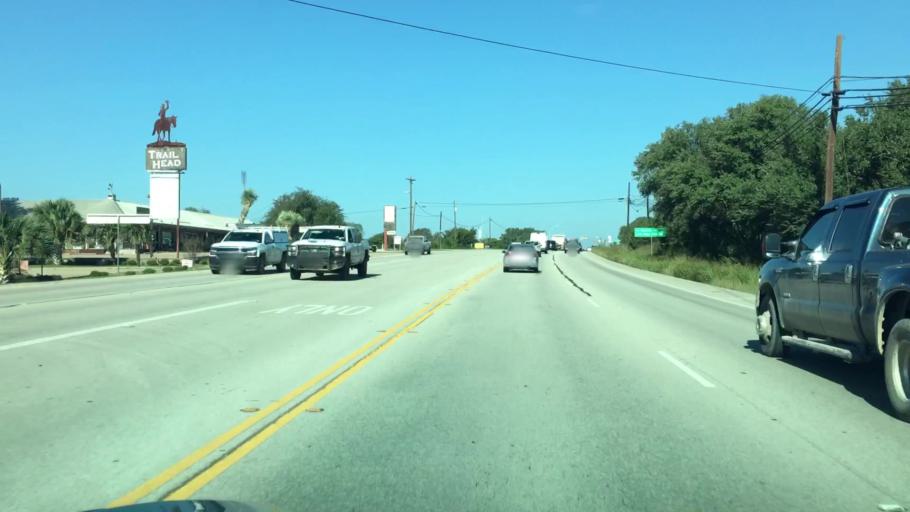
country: US
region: Texas
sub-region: Hays County
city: Dripping Springs
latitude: 30.1949
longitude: -98.1026
